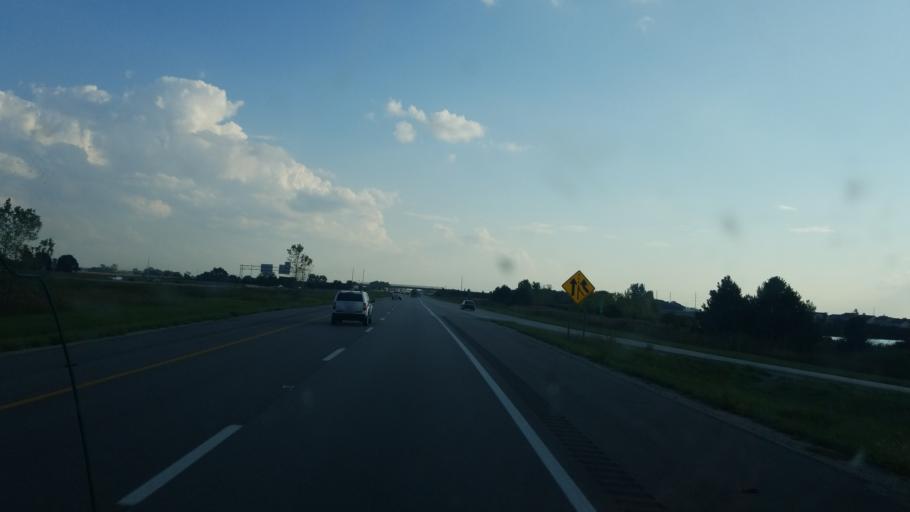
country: US
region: Ohio
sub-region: Wood County
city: Perrysburg
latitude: 41.5287
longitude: -83.6221
